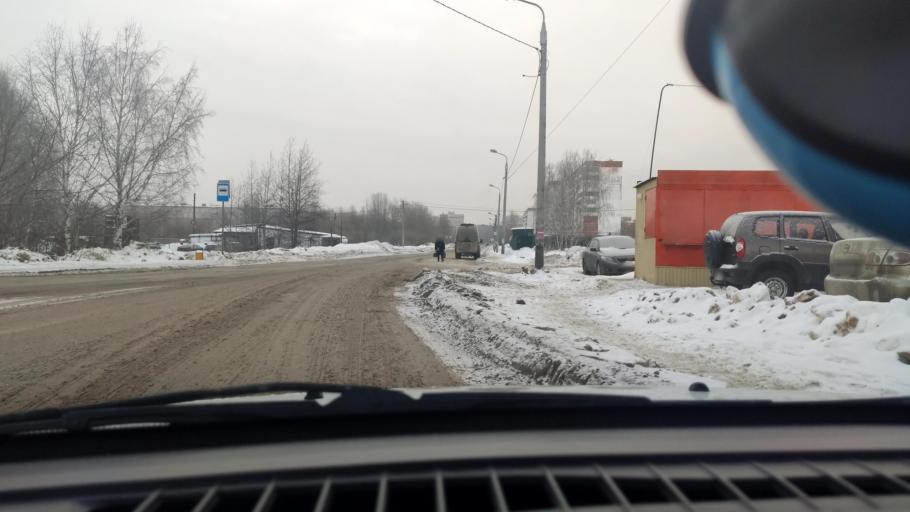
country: RU
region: Perm
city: Overyata
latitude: 58.0283
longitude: 55.8286
